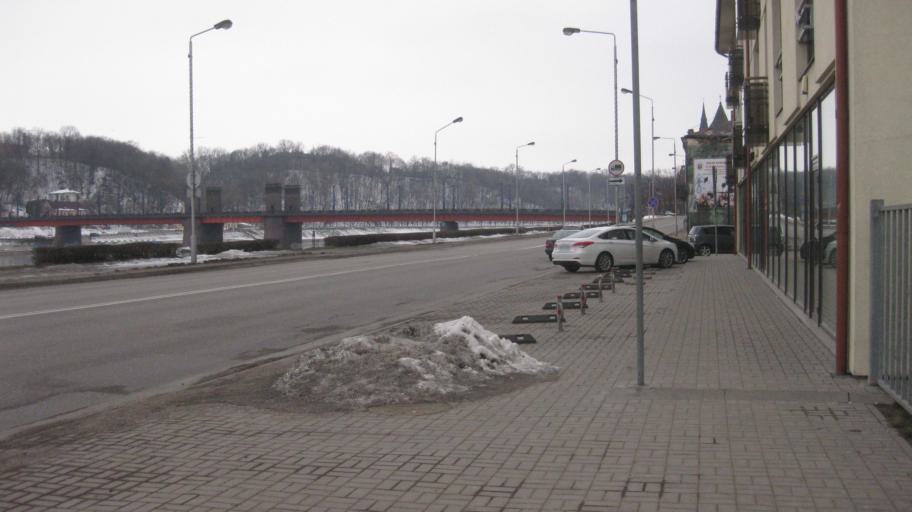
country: LT
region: Kauno apskritis
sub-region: Kaunas
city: Kaunas
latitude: 54.8948
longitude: 23.8921
